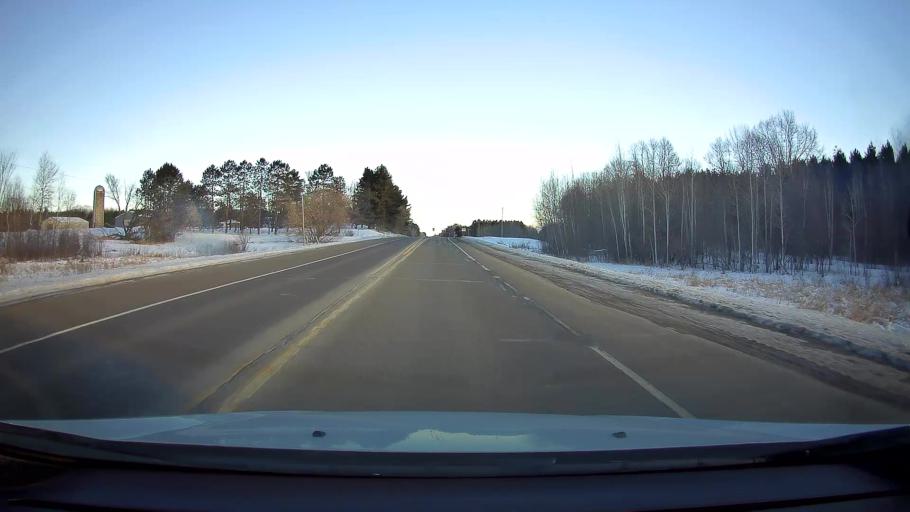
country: US
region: Wisconsin
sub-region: Barron County
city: Cumberland
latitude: 45.5540
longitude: -92.0172
